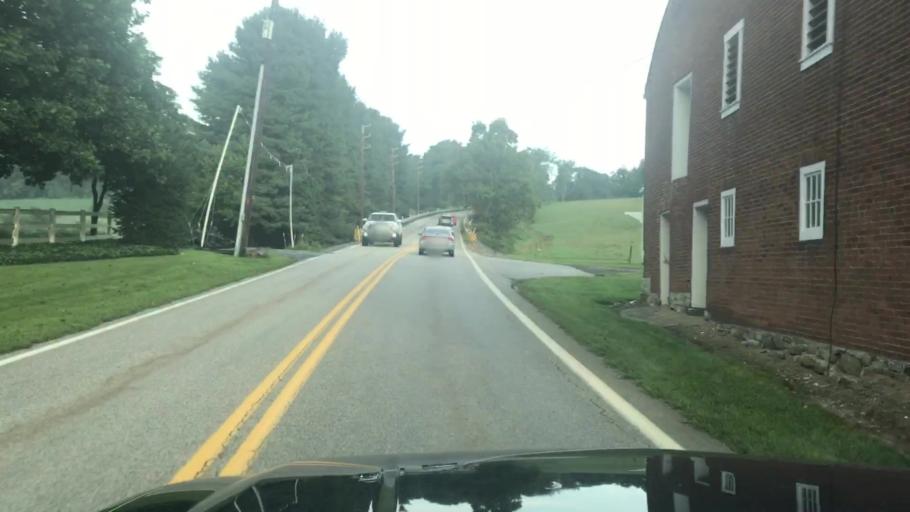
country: US
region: Pennsylvania
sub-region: Cumberland County
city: Shiremanstown
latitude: 40.1978
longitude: -76.9458
